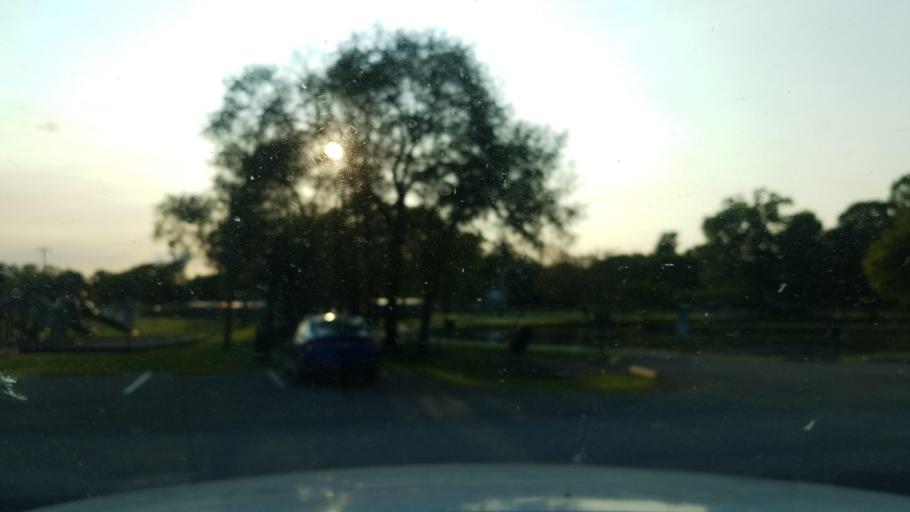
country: US
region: Illinois
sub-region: Saline County
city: Harrisburg
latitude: 37.7345
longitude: -88.5546
